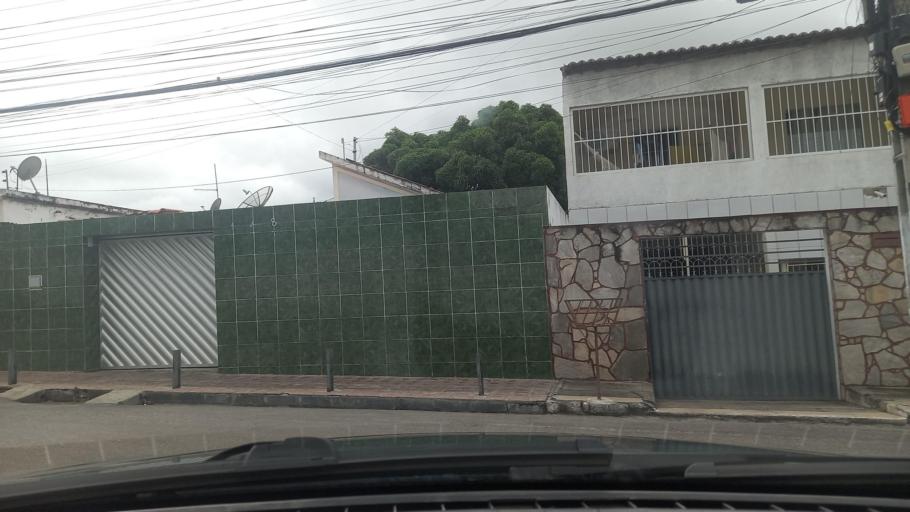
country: BR
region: Alagoas
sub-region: Delmiro Gouveia
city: Delmiro Gouveia
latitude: -9.3896
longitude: -37.9973
